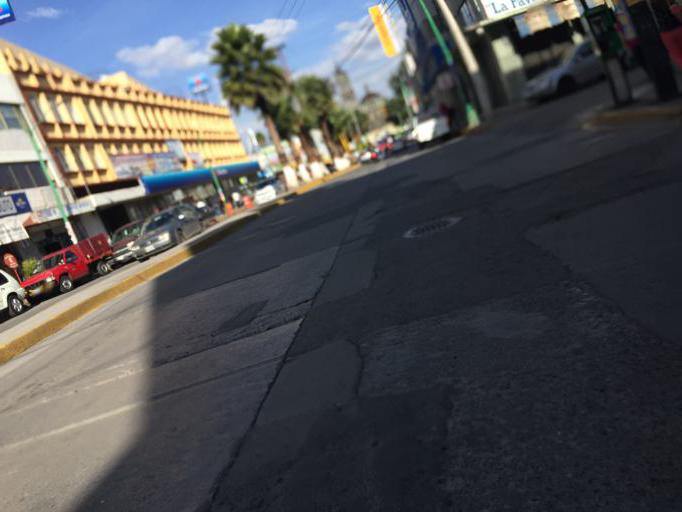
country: MX
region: Mexico
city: Cuautitlan
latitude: 19.6694
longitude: -99.1823
